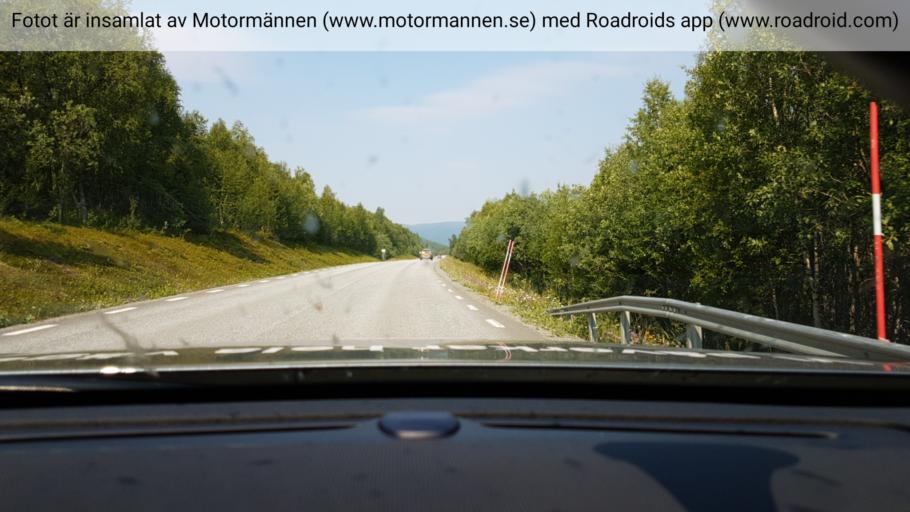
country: NO
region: Nordland
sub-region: Rana
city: Mo i Rana
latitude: 65.7164
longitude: 15.2039
